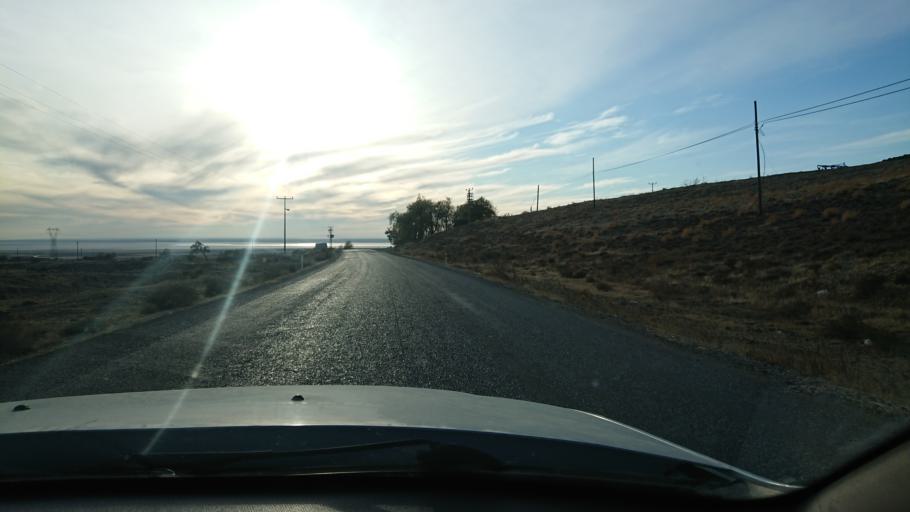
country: TR
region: Ankara
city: Sereflikochisar
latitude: 38.7458
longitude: 33.6819
